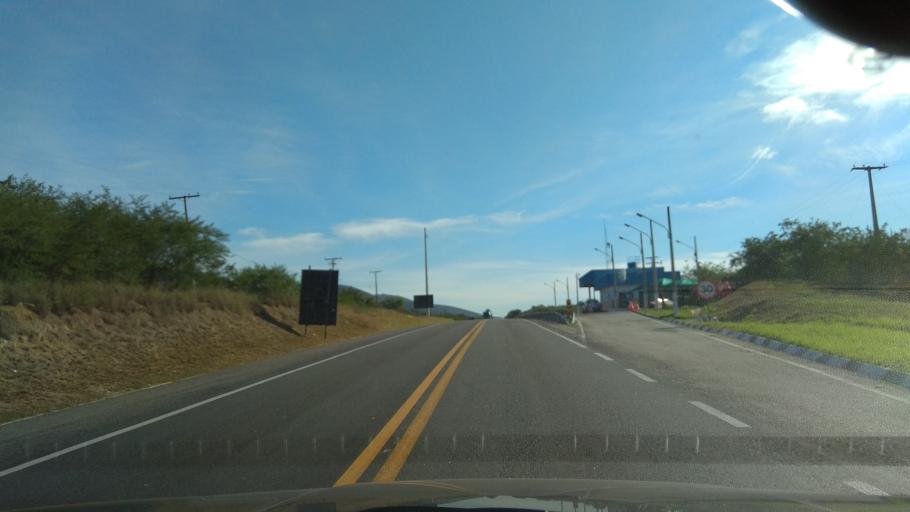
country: BR
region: Bahia
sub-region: Jequie
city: Jequie
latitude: -13.8084
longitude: -40.1121
